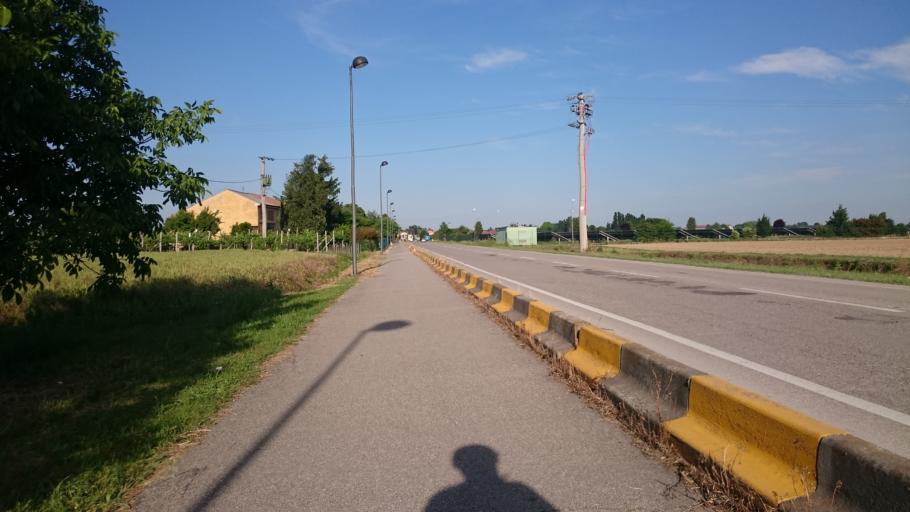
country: IT
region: Lombardy
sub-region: Provincia di Mantova
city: Villimpenta
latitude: 45.1449
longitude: 11.0162
